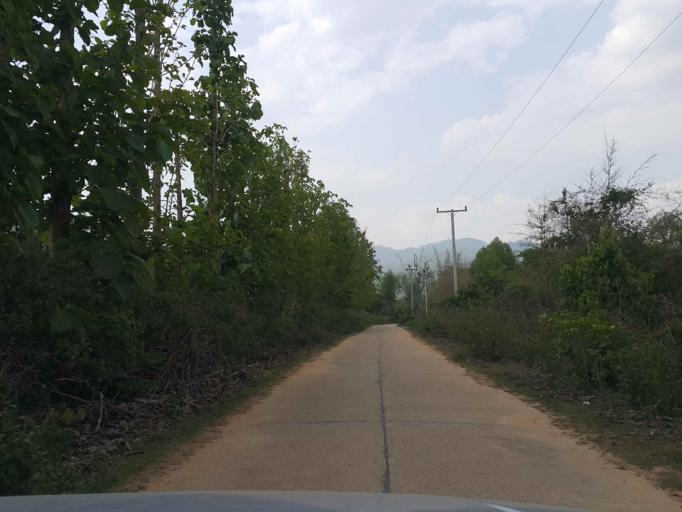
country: TH
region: Chiang Mai
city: Wiang Haeng
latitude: 19.4015
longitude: 98.7222
